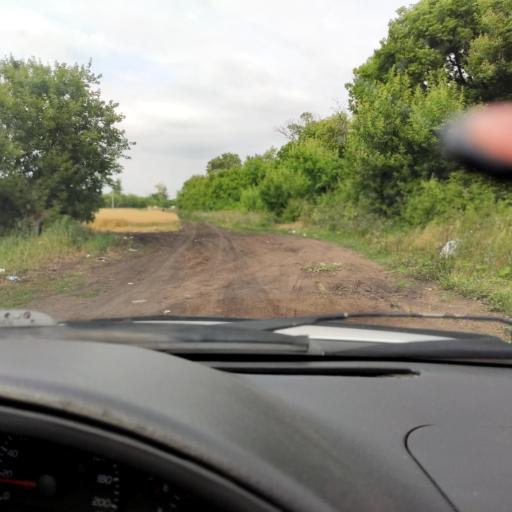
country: RU
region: Bashkortostan
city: Alekseyevka
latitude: 54.7300
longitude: 55.0016
